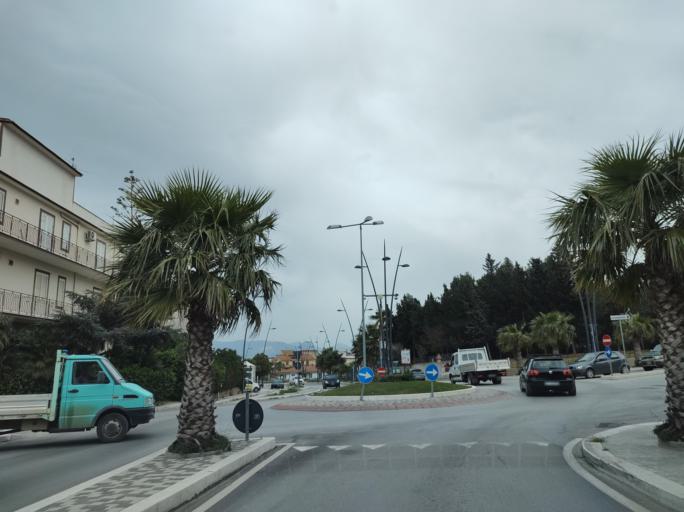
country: IT
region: Sicily
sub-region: Trapani
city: Castellammare del Golfo
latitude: 38.0174
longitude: 12.8870
